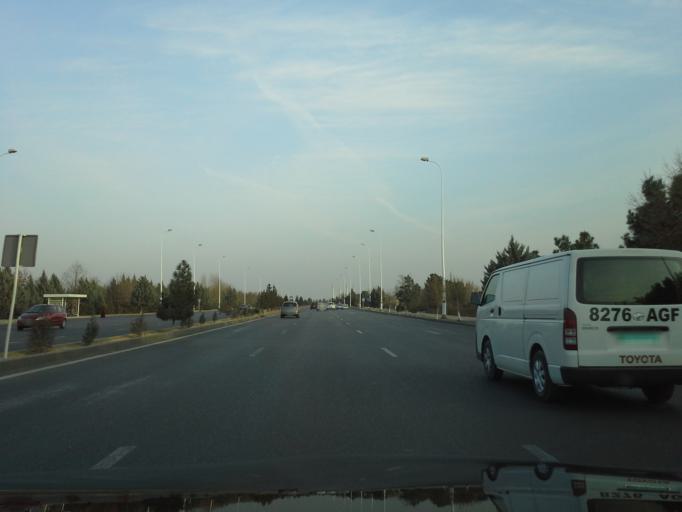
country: TM
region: Ahal
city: Abadan
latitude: 38.0320
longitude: 58.2275
